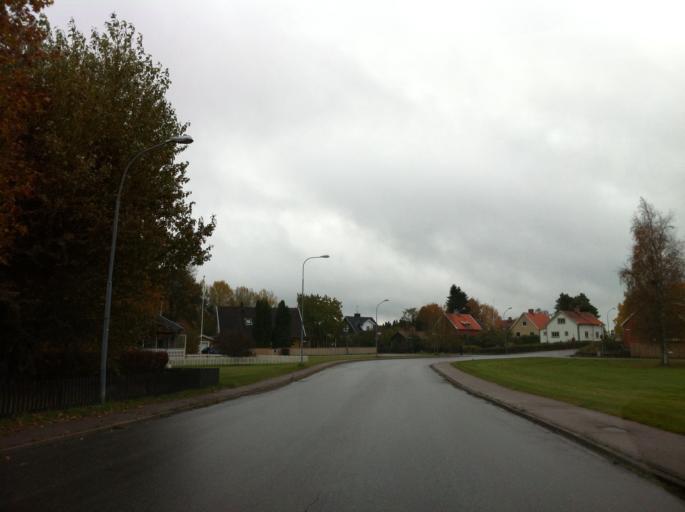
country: SE
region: Uppsala
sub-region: Osthammars Kommun
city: OEsthammar
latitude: 60.2676
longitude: 18.3675
